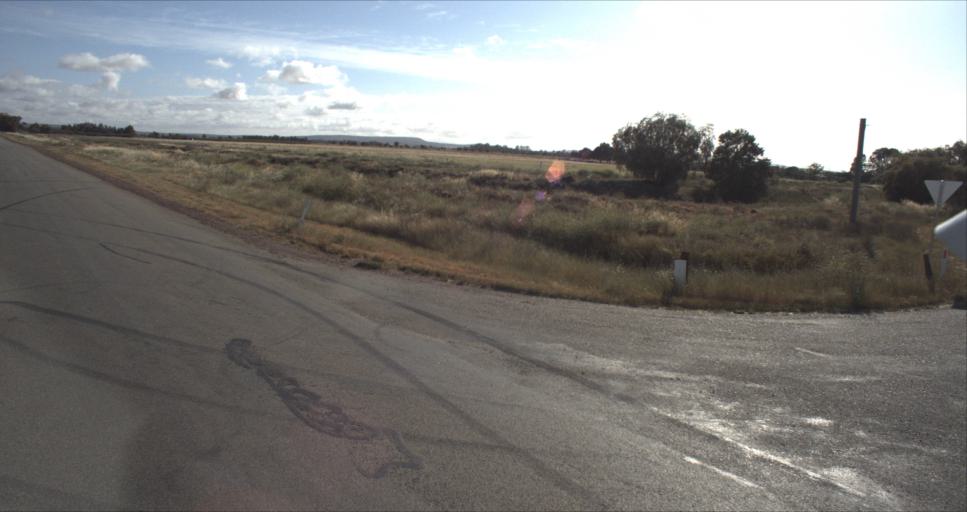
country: AU
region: New South Wales
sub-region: Leeton
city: Leeton
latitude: -34.5267
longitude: 146.3896
